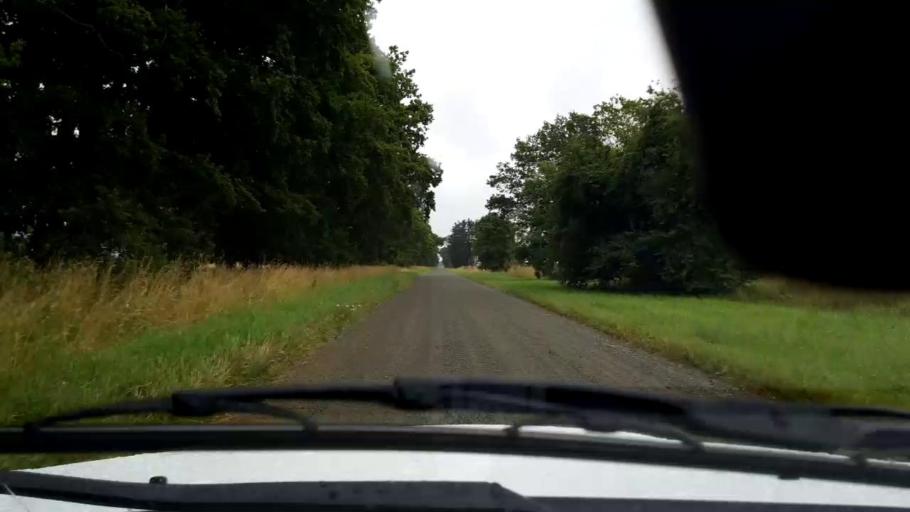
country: NZ
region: Canterbury
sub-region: Timaru District
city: Pleasant Point
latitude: -44.2178
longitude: 171.2812
